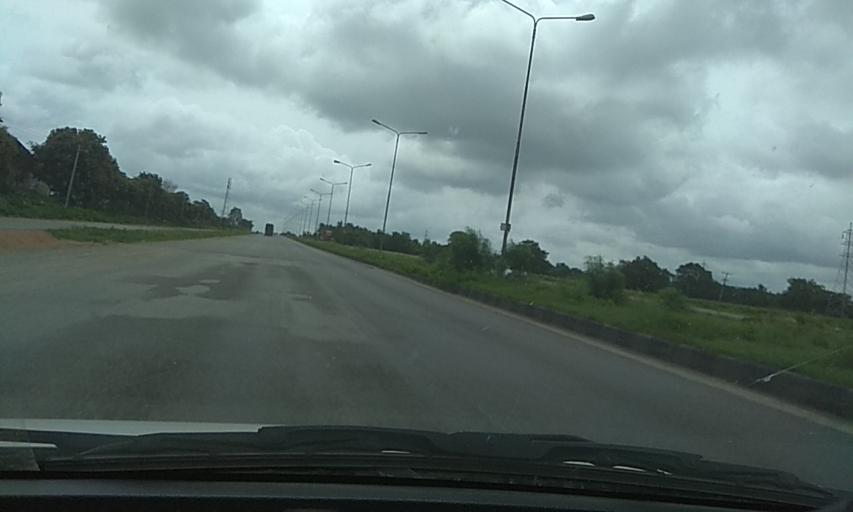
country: IN
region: Karnataka
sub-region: Davanagere
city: Mayakonda
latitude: 14.3751
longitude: 76.1088
